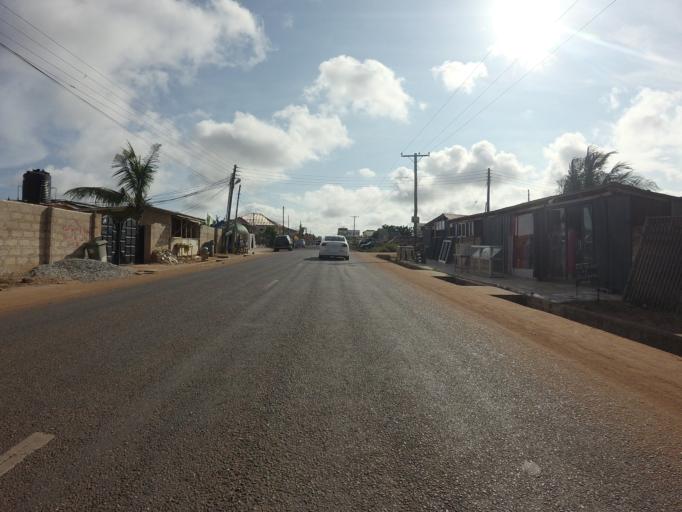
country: GH
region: Greater Accra
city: Teshi Old Town
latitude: 5.5874
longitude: -0.1391
